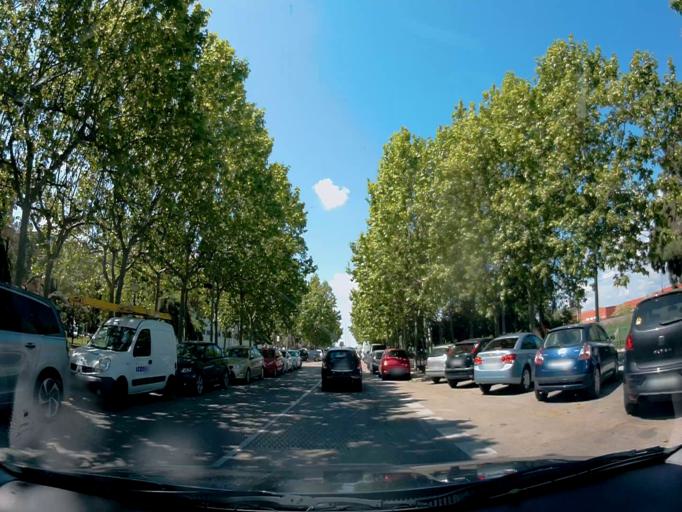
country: ES
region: Madrid
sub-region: Provincia de Madrid
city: Alcorcon
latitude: 40.3486
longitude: -3.8334
